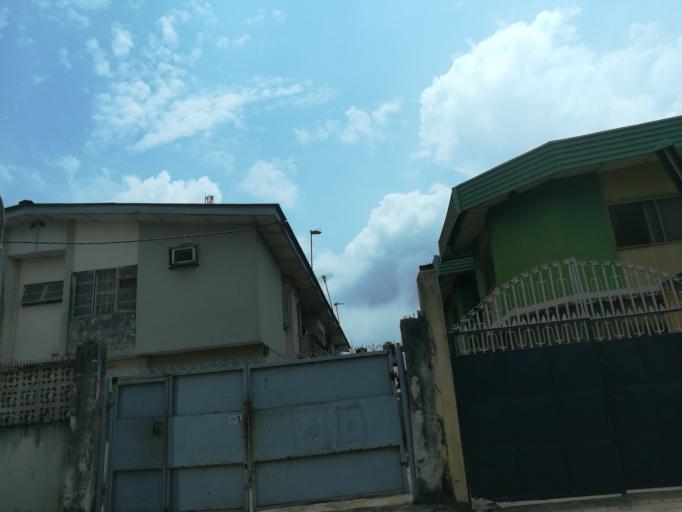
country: NG
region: Lagos
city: Oshodi
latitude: 6.5510
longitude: 3.3267
